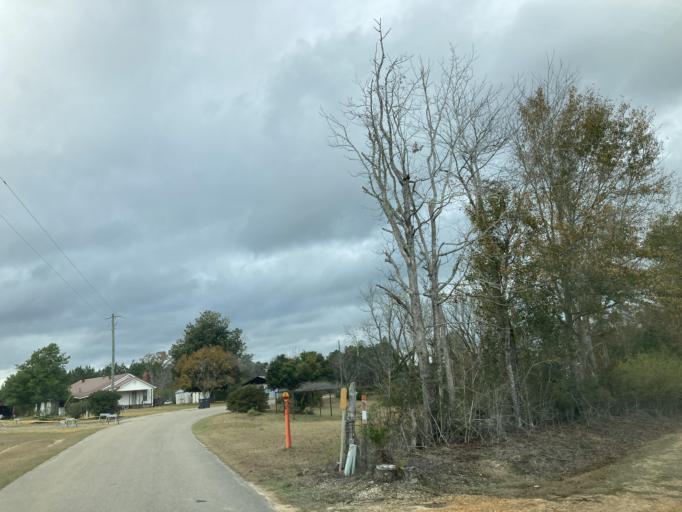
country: US
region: Mississippi
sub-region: Lamar County
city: Purvis
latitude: 31.1435
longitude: -89.5181
